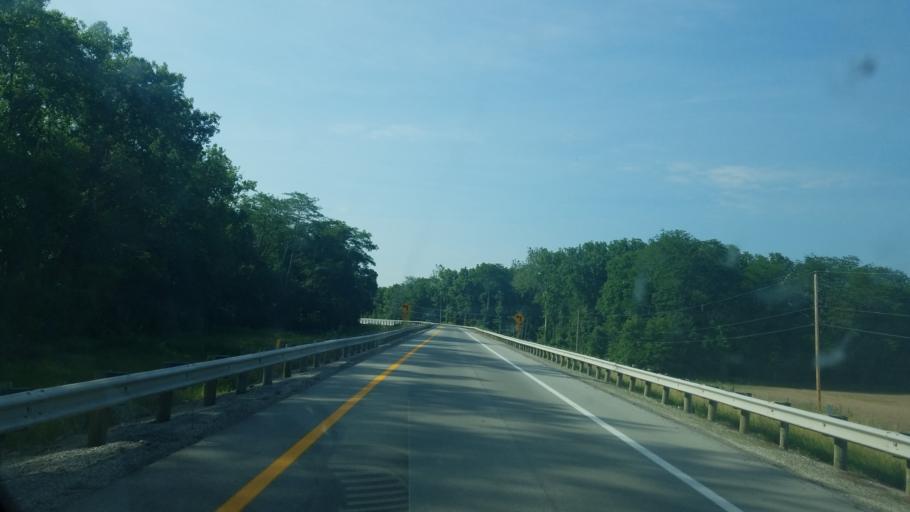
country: US
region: Ohio
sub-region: Hancock County
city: Findlay
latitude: 40.9910
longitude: -83.6524
